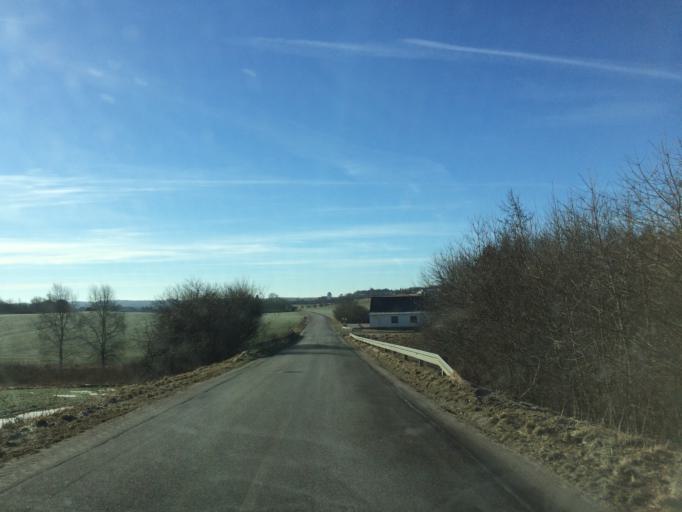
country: DK
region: North Denmark
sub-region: Vesthimmerland Kommune
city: Alestrup
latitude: 56.6010
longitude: 9.6299
